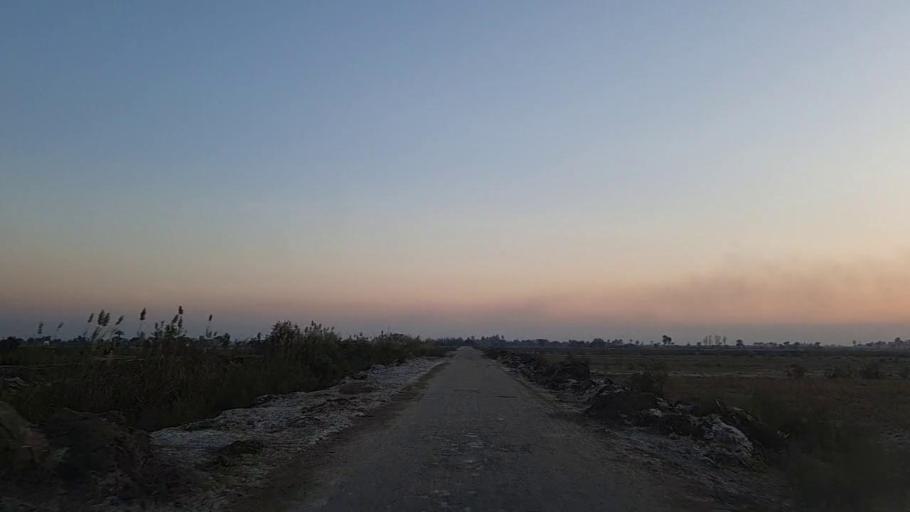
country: PK
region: Sindh
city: Bandhi
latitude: 26.5923
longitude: 68.3360
